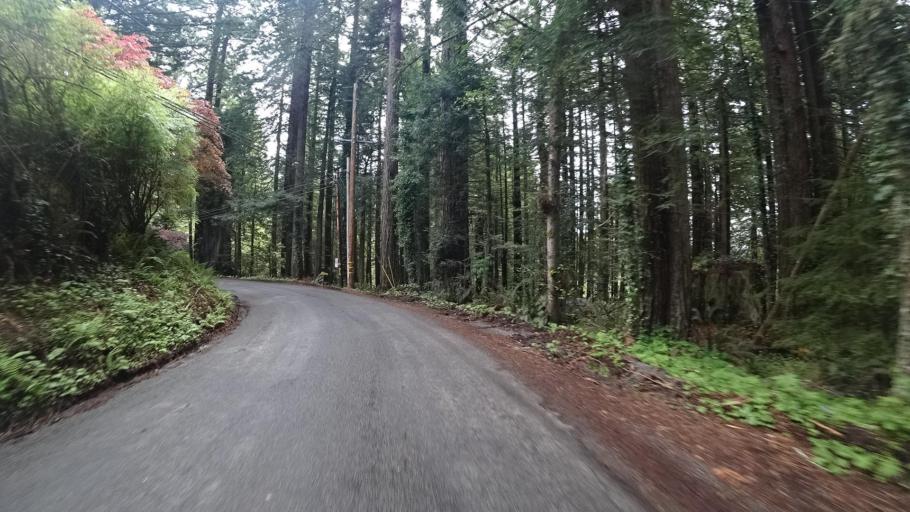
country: US
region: California
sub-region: Humboldt County
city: Bayside
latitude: 40.8552
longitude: -124.0344
